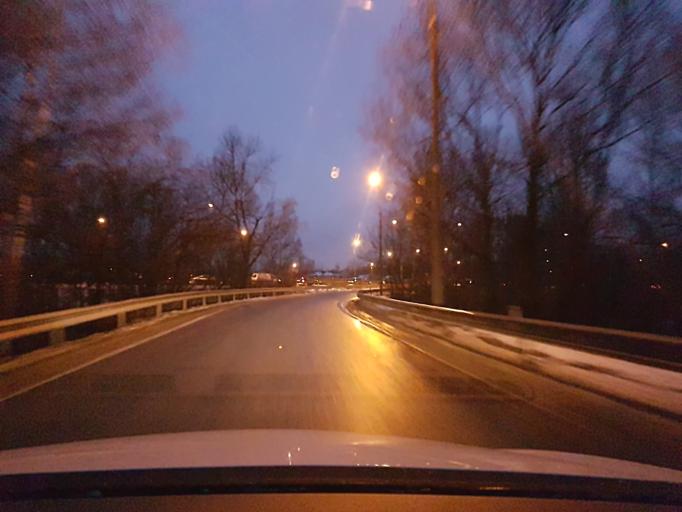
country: RU
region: Moskovskaya
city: Sheremet'yevskiy
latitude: 55.9767
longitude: 37.5258
